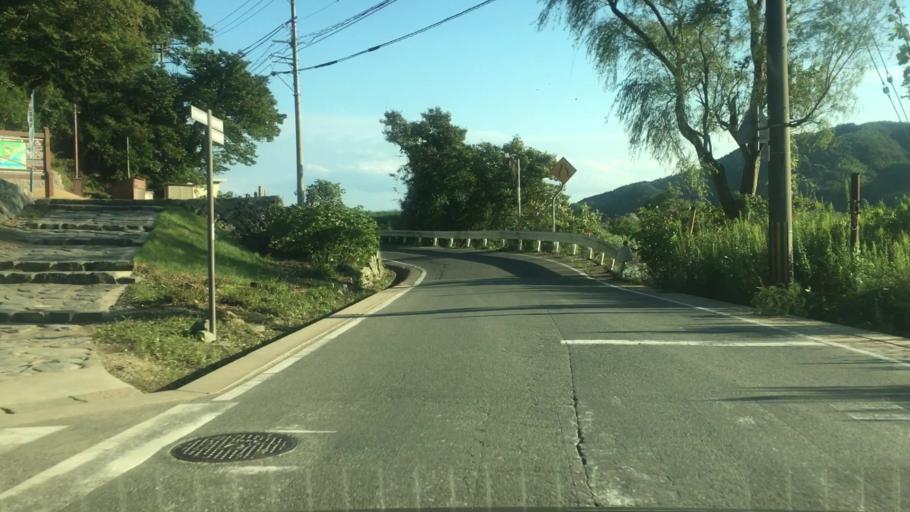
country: JP
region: Hyogo
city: Toyooka
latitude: 35.5884
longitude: 134.8038
